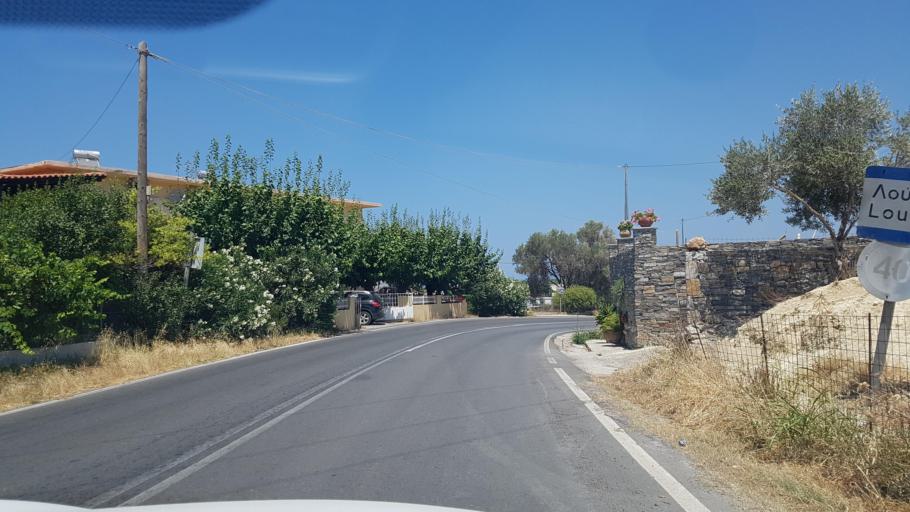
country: GR
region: Crete
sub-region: Nomos Rethymnis
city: Agia Foteini
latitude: 35.3542
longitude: 24.5880
